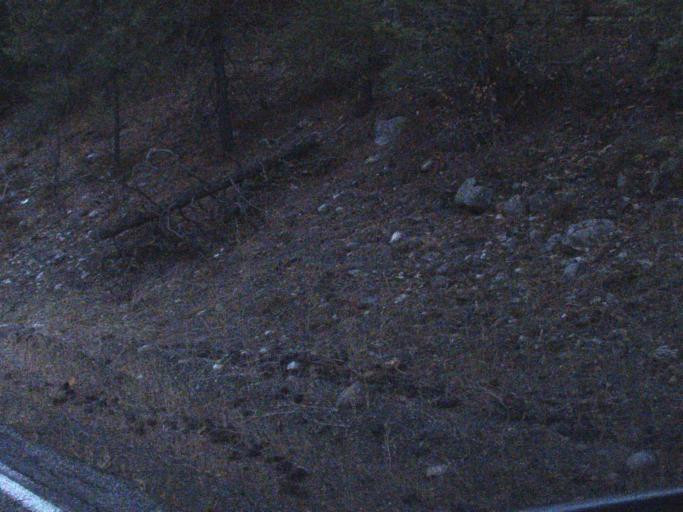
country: US
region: Washington
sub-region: Ferry County
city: Republic
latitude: 48.4281
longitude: -118.7282
